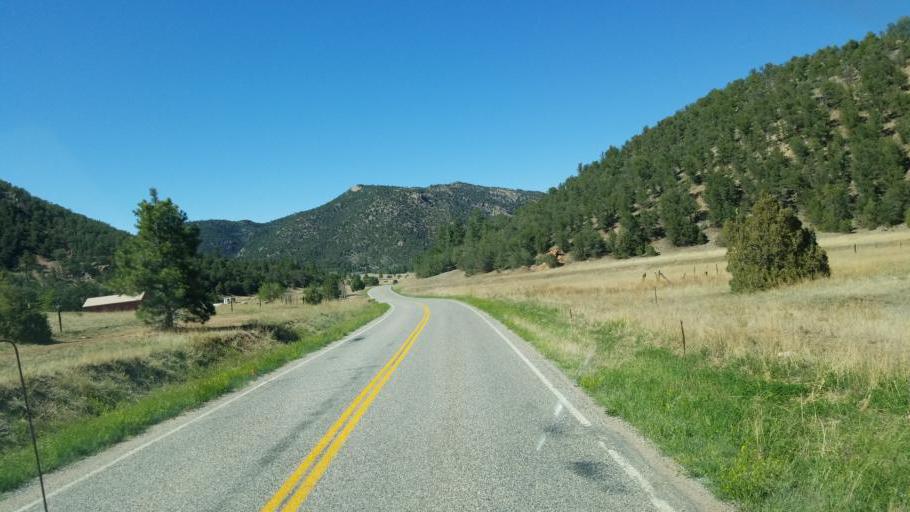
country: US
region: Colorado
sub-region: Fremont County
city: Canon City
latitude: 38.3760
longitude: -105.4563
